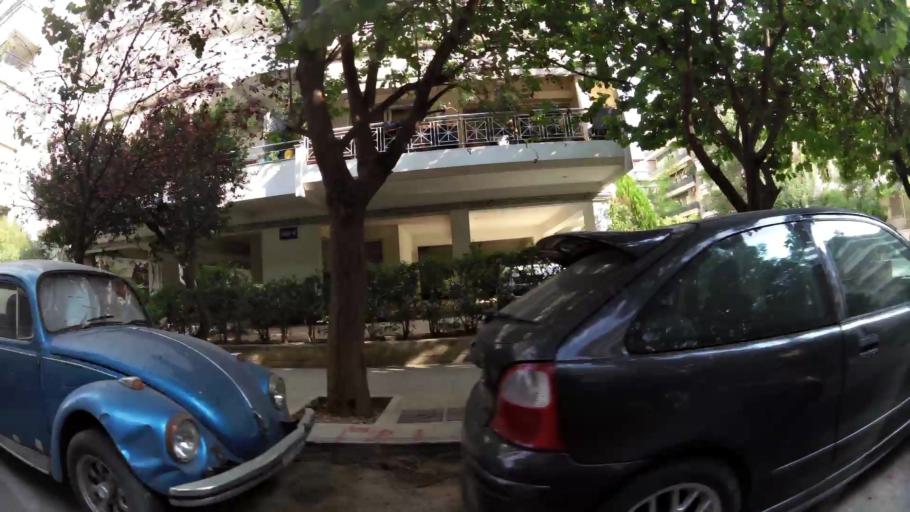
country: GR
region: Attica
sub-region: Nomarchia Athinas
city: Nea Smyrni
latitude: 37.9421
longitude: 23.7146
